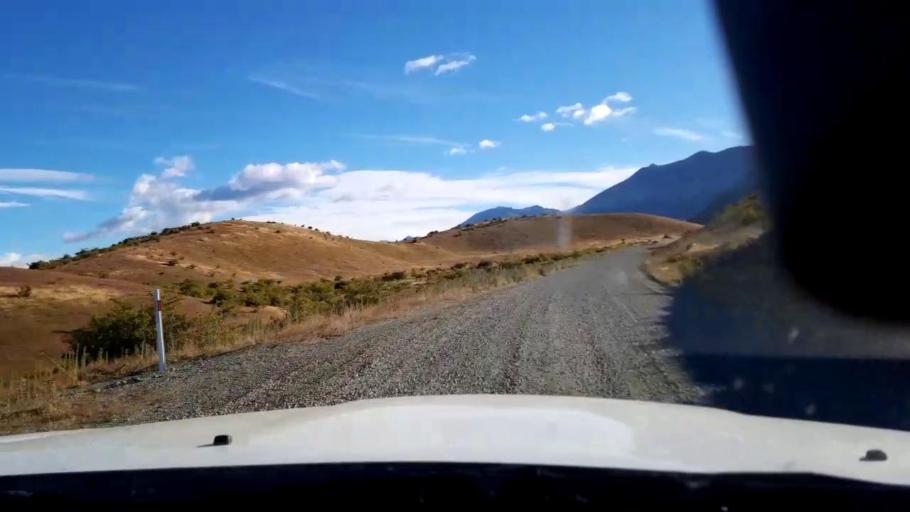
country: NZ
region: Canterbury
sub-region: Timaru District
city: Pleasant Point
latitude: -43.9671
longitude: 170.5173
